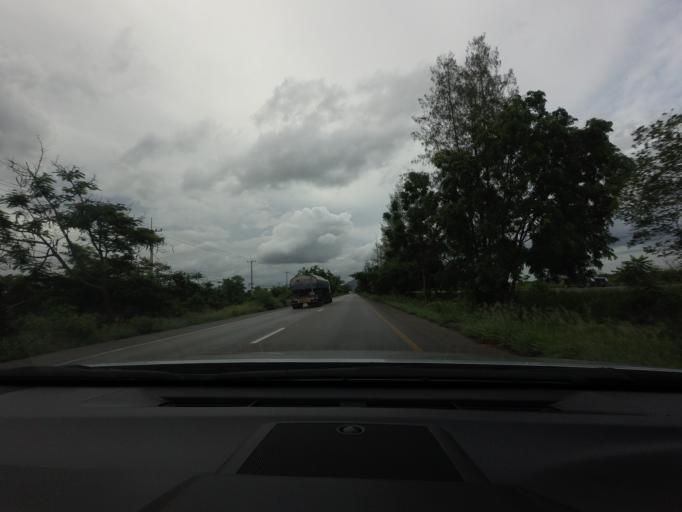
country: TH
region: Phetchaburi
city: Cha-am
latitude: 12.7609
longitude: 99.9335
